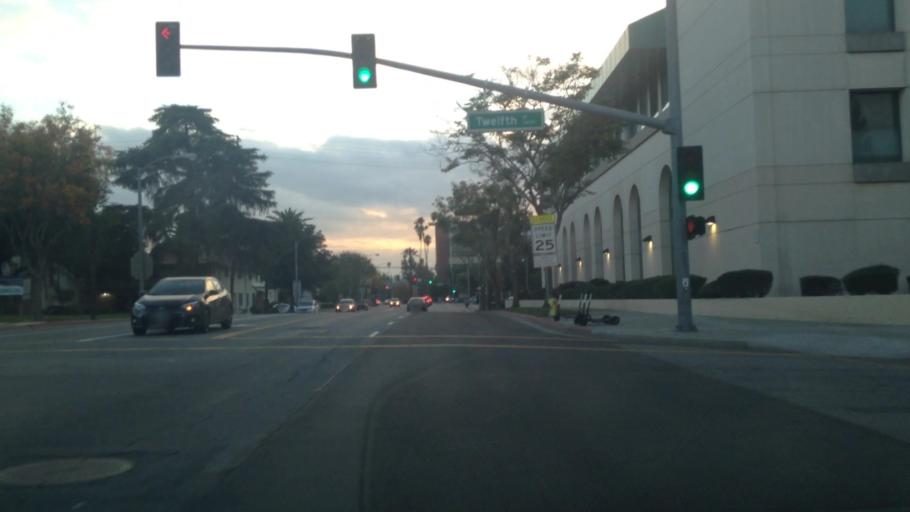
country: US
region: California
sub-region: Riverside County
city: Riverside
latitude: 33.9765
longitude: -117.3736
